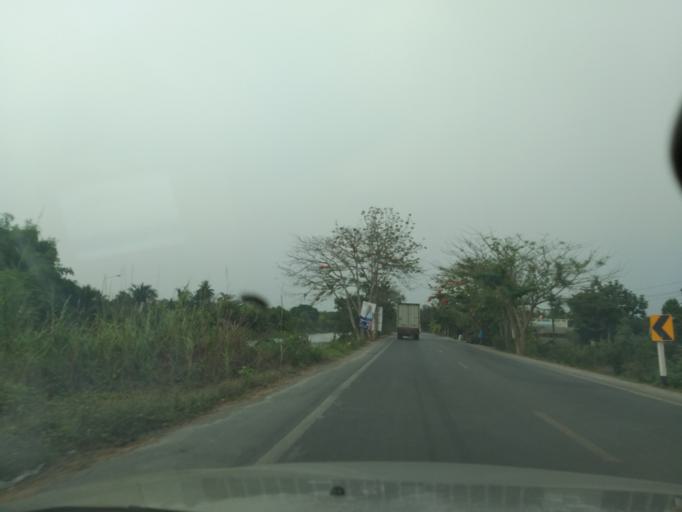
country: TH
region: Bangkok
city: Nong Chok
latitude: 13.9435
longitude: 100.8950
